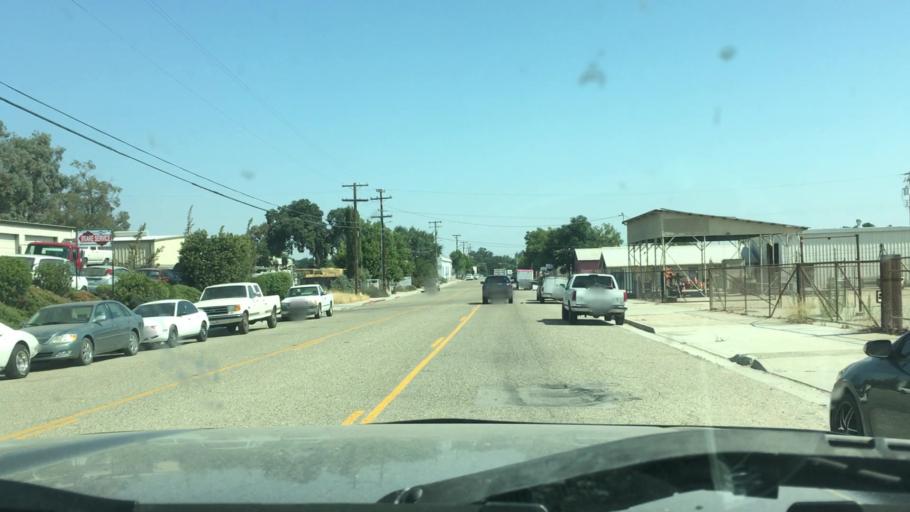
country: US
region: California
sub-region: San Luis Obispo County
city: Paso Robles
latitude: 35.6240
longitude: -120.6854
